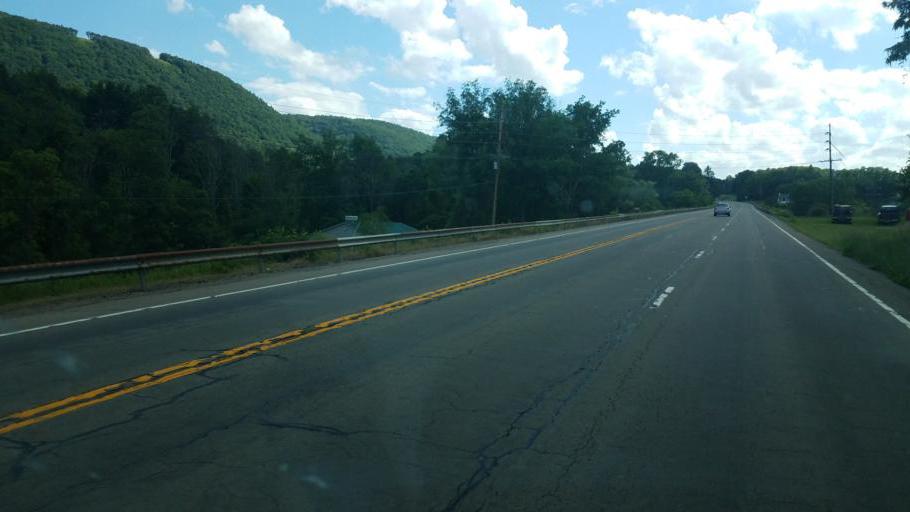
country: US
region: New York
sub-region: Steuben County
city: Bath
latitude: 42.3859
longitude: -77.2633
